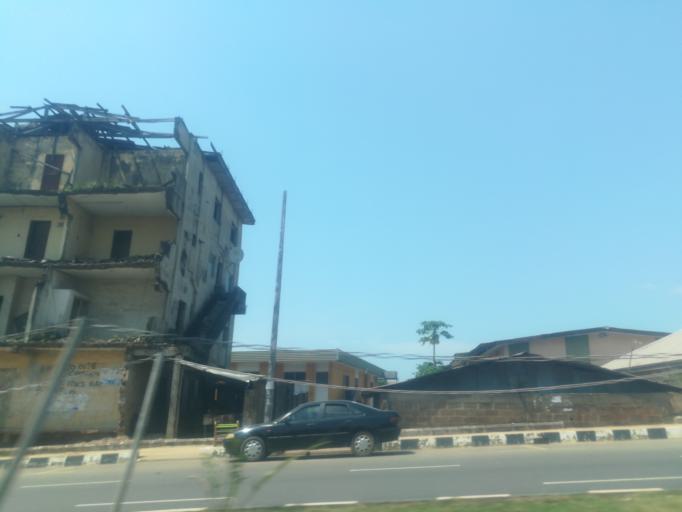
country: NG
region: Ogun
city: Abeokuta
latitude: 7.1539
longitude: 3.3661
